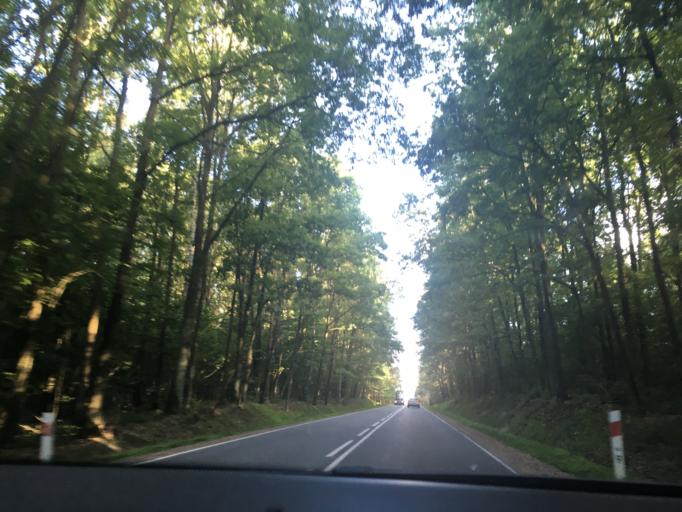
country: PL
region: Masovian Voivodeship
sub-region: Powiat losicki
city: Sarnaki
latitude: 52.3415
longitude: 22.8758
